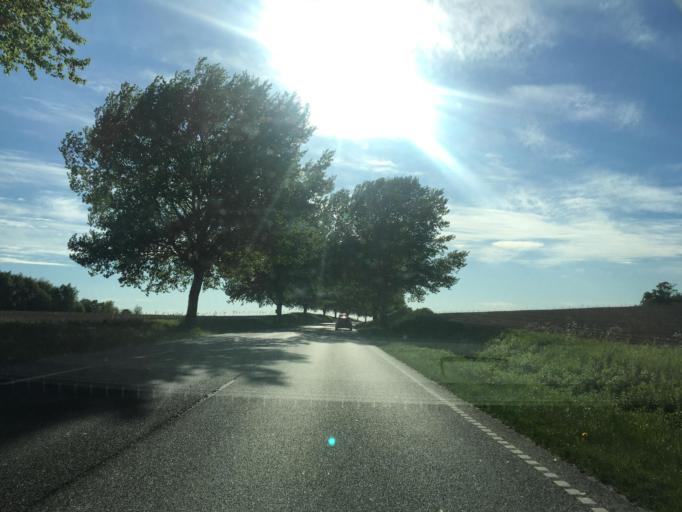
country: DK
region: Capital Region
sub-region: Frederikssund Kommune
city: Slangerup
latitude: 55.8349
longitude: 12.1797
